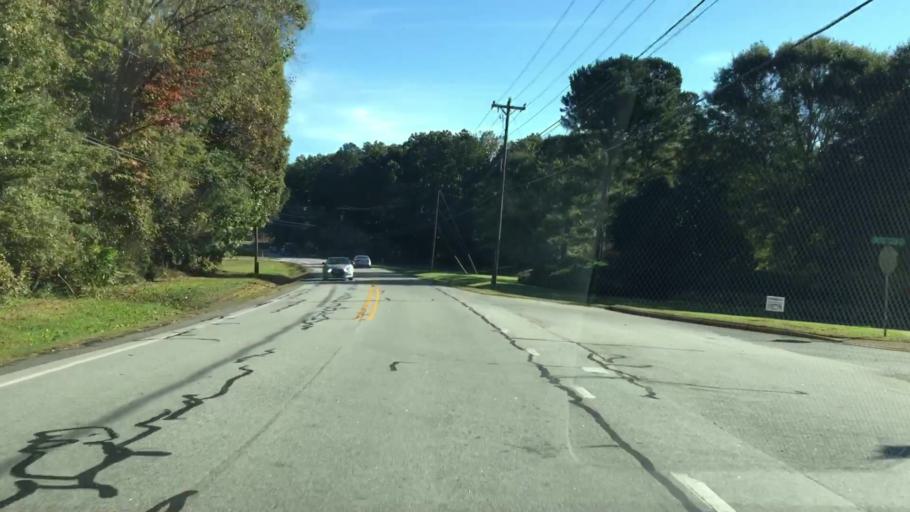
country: US
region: North Carolina
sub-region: Rowan County
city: Salisbury
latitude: 35.6611
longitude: -80.5350
